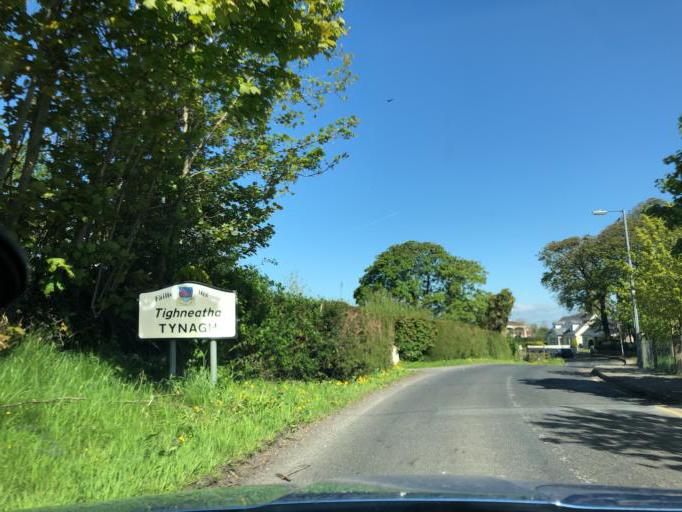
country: IE
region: Connaught
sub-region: County Galway
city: Portumna
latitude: 53.1428
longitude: -8.3683
